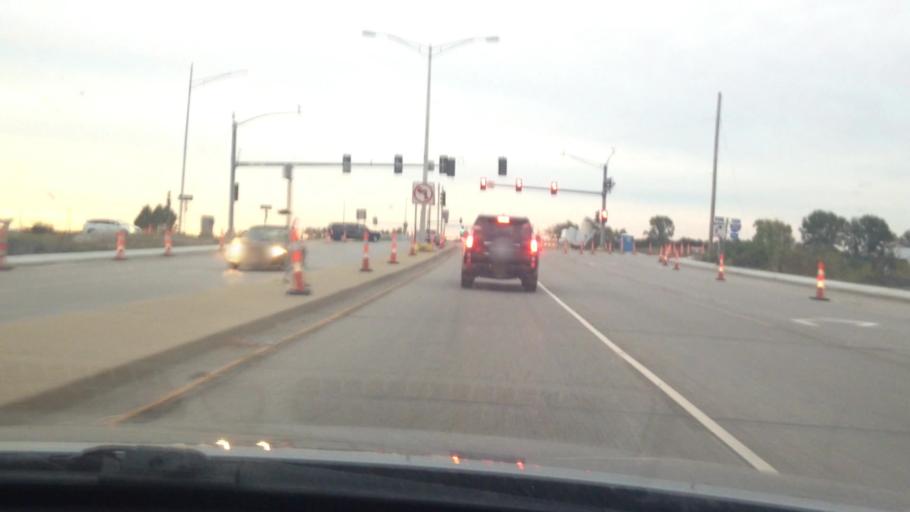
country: US
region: Missouri
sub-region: Jackson County
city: Lees Summit
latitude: 38.9429
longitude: -94.3782
